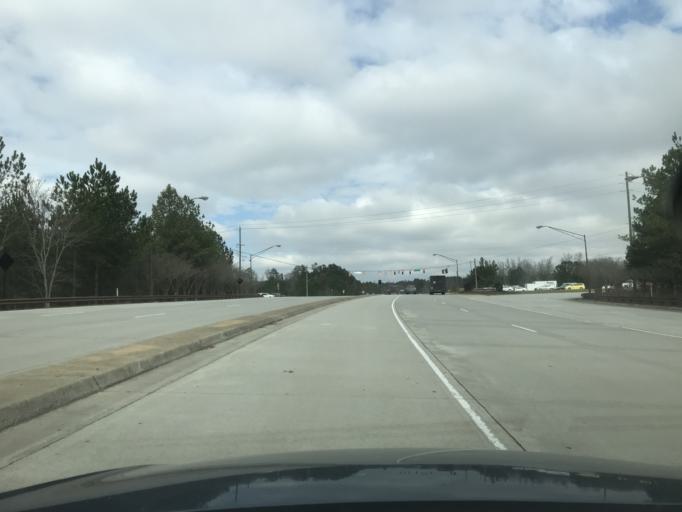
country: US
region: Georgia
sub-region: Columbia County
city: Grovetown
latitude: 33.4394
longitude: -82.1184
